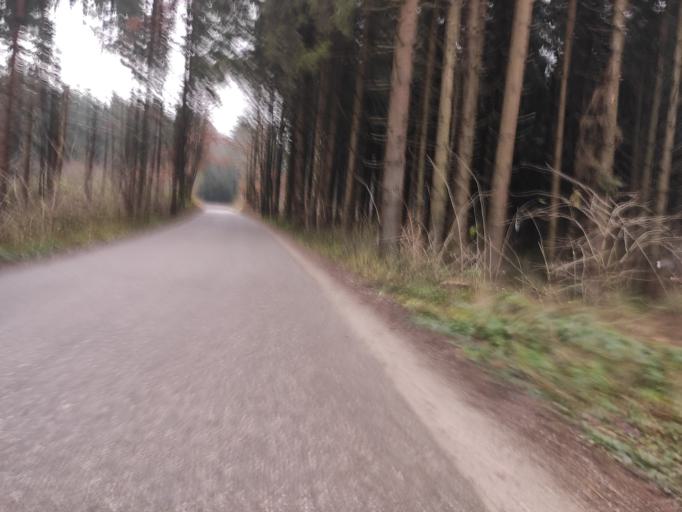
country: AT
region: Salzburg
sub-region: Politischer Bezirk Salzburg-Umgebung
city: Neumarkt am Wallersee
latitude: 47.9711
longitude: 13.2309
